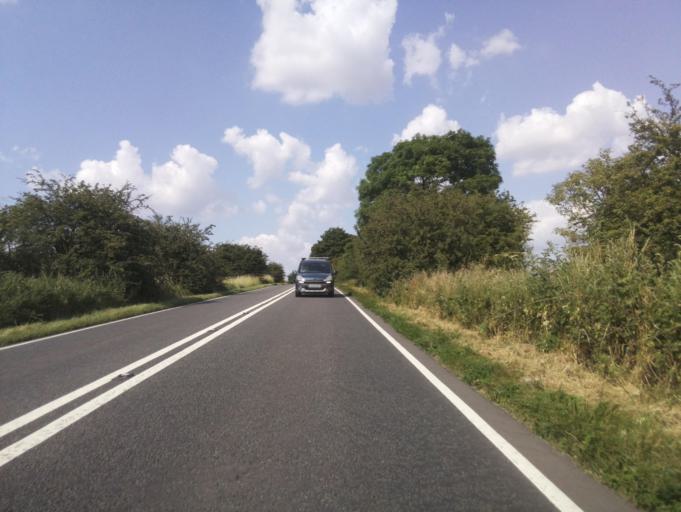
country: GB
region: England
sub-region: Gloucestershire
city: Northleach
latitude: 51.8580
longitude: -1.8016
